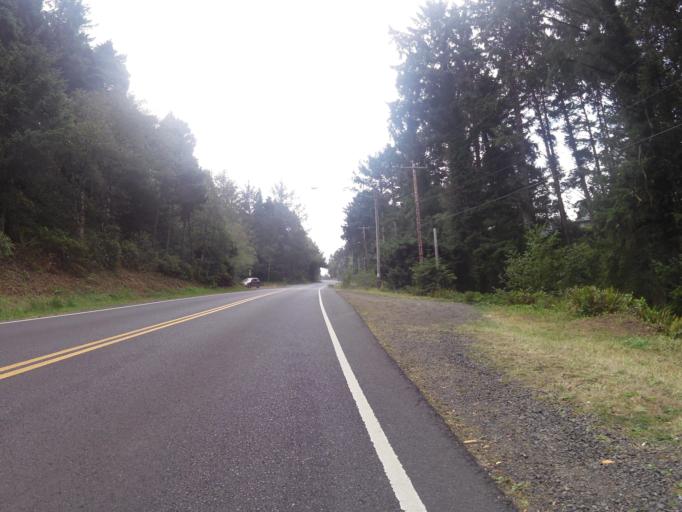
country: US
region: Oregon
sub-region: Lincoln County
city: Newport
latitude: 44.6568
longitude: -124.0559
